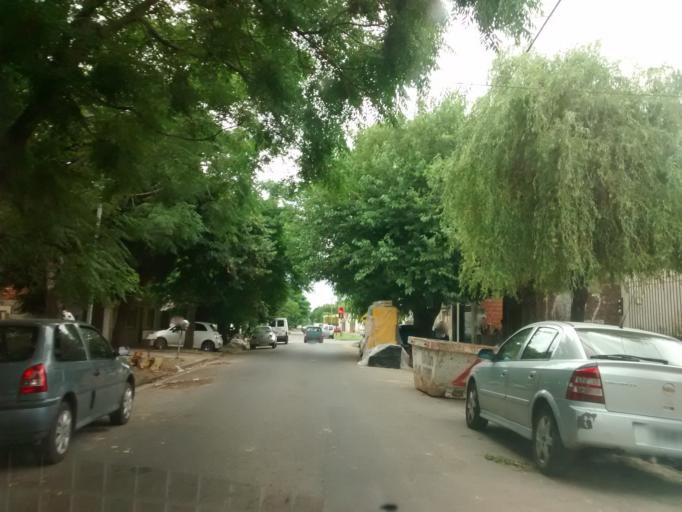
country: AR
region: Buenos Aires
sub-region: Partido de La Plata
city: La Plata
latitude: -34.9210
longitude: -57.9128
